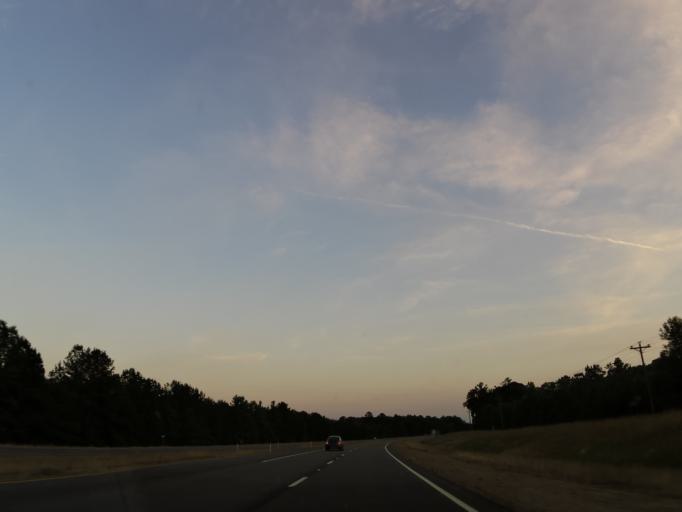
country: US
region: Mississippi
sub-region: Kemper County
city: De Kalb
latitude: 32.8077
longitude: -88.4550
